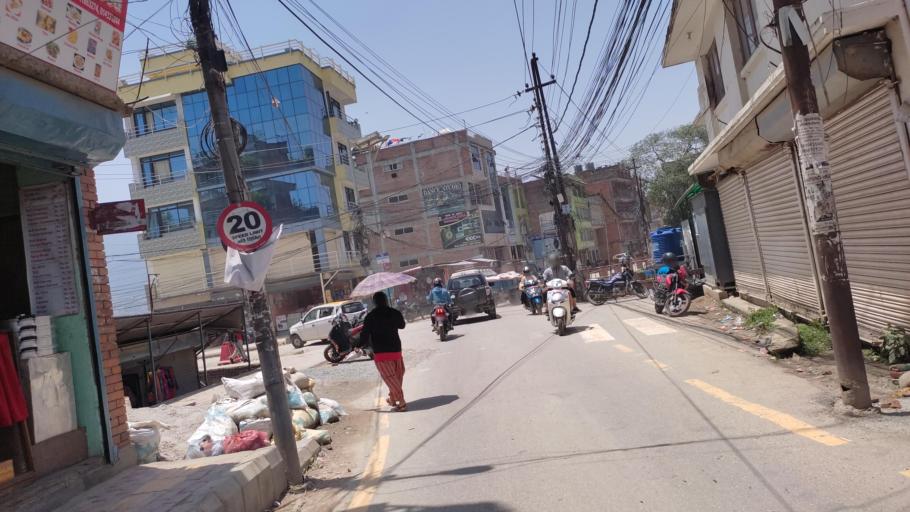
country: NP
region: Central Region
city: Kirtipur
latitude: 27.6780
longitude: 85.2740
